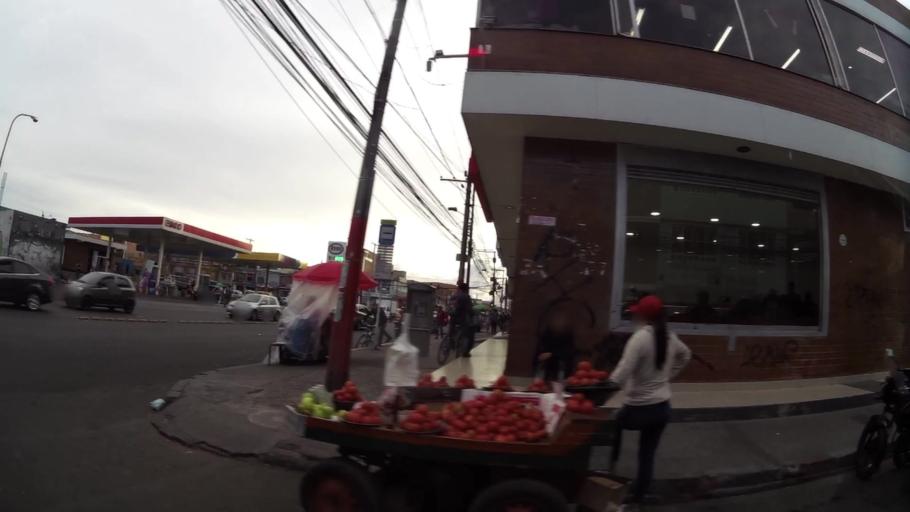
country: CO
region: Cundinamarca
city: Soacha
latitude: 4.6204
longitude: -74.1606
